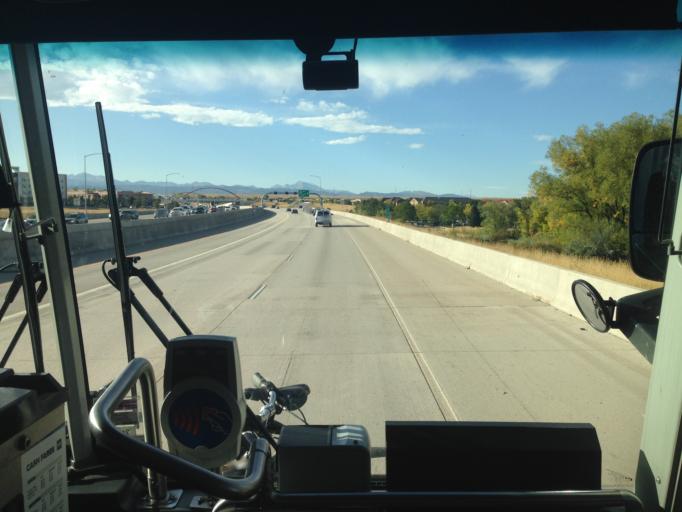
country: US
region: Colorado
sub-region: Boulder County
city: Superior
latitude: 39.9547
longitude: -105.1587
